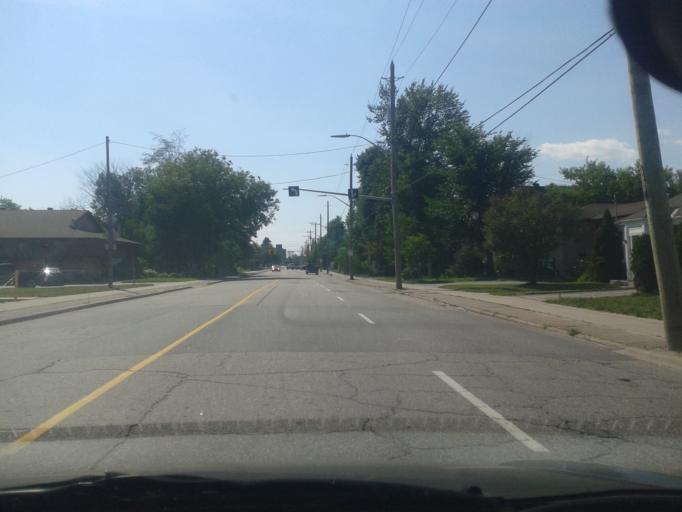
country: CA
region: Ontario
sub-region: Nipissing District
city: North Bay
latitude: 46.3180
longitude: -79.4471
